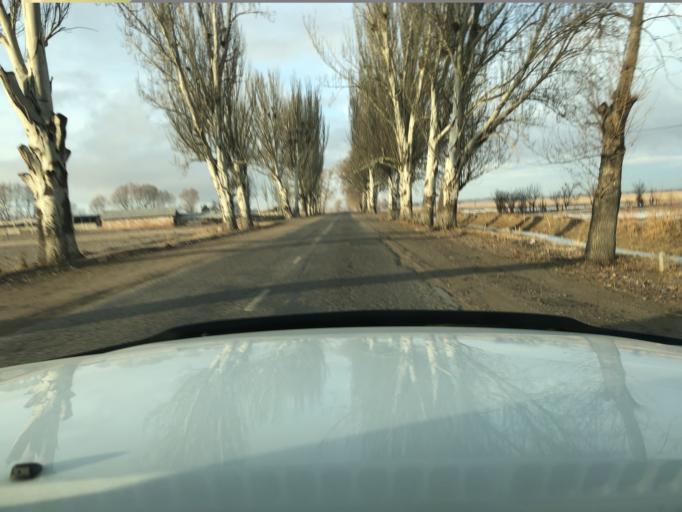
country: KG
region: Ysyk-Koel
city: Karakol
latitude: 42.4770
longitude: 78.3287
